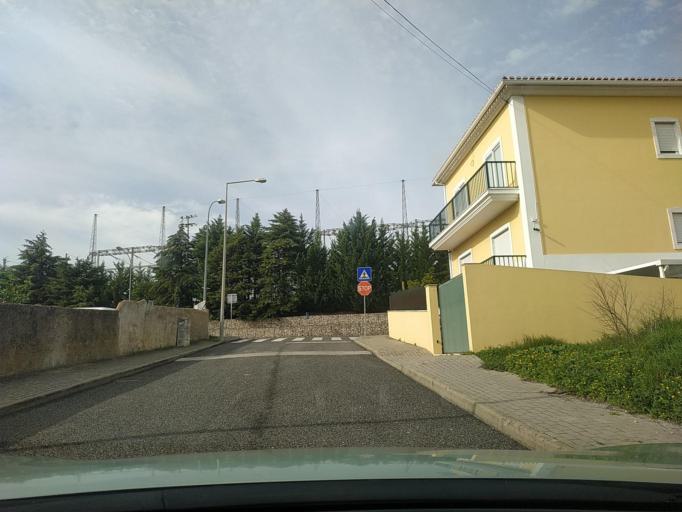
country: PT
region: Lisbon
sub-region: Sintra
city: Belas
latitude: 38.7766
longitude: -9.2384
